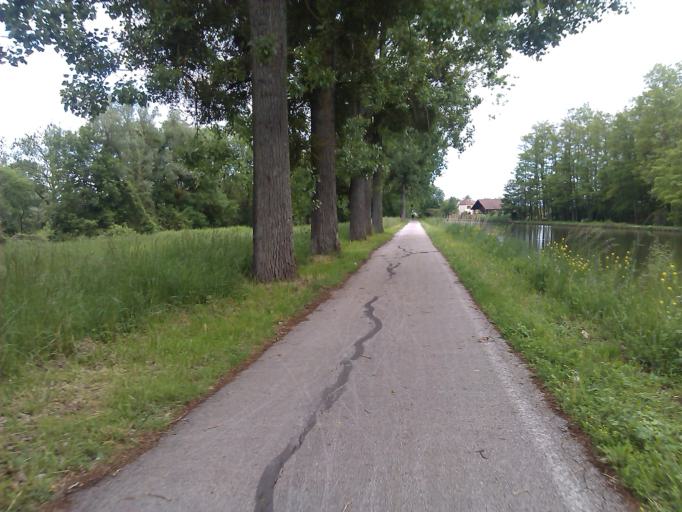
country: FR
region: Bourgogne
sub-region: Departement de Saone-et-Loire
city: Virey-le-Grand
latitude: 46.8270
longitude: 4.8505
